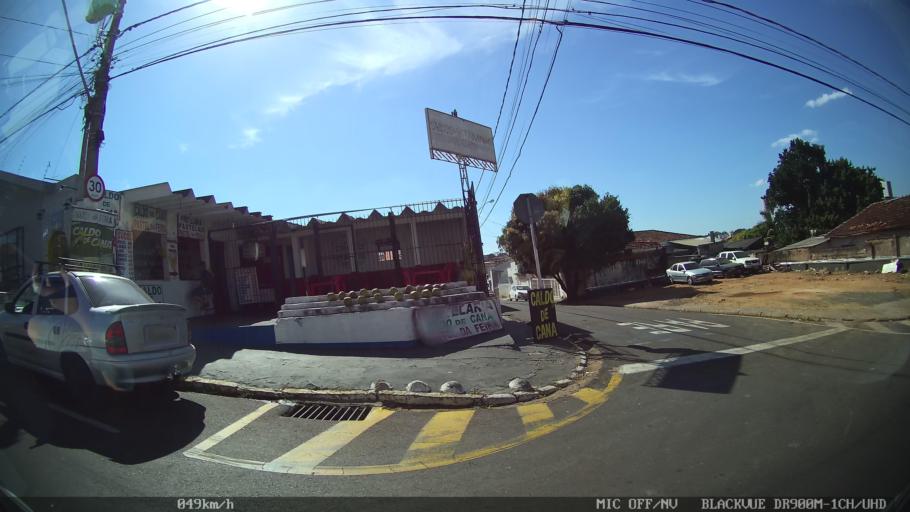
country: BR
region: Sao Paulo
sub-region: Franca
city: Franca
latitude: -20.5331
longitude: -47.4076
